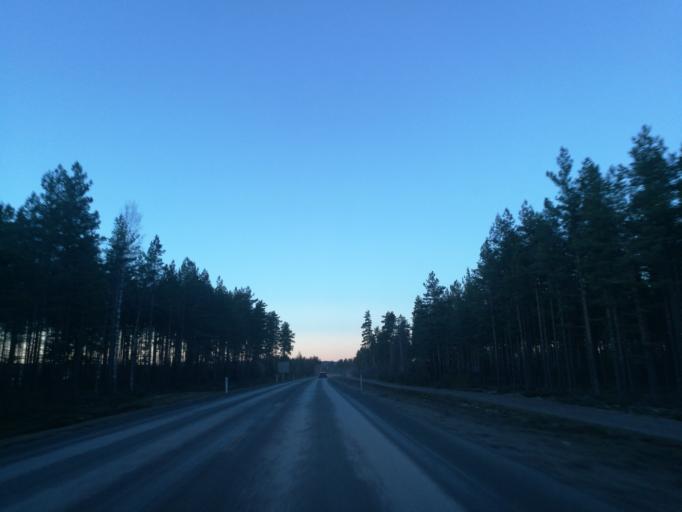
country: NO
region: Hedmark
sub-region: Eidskog
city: Skotterud
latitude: 59.9603
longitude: 12.1583
